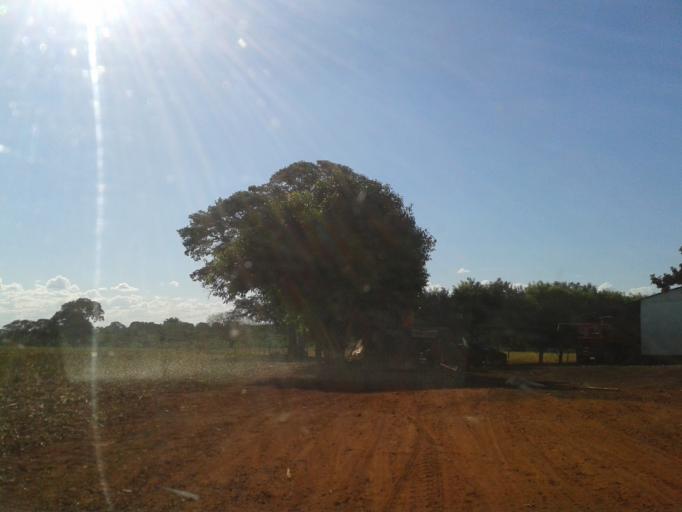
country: BR
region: Minas Gerais
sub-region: Centralina
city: Centralina
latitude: -18.5948
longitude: -49.2627
